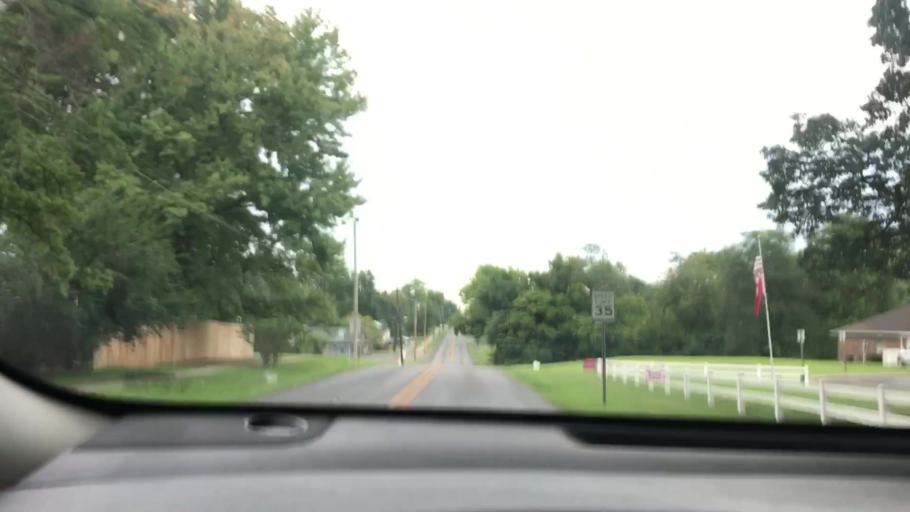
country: US
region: Kentucky
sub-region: Calloway County
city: Murray
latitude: 36.6029
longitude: -88.3201
